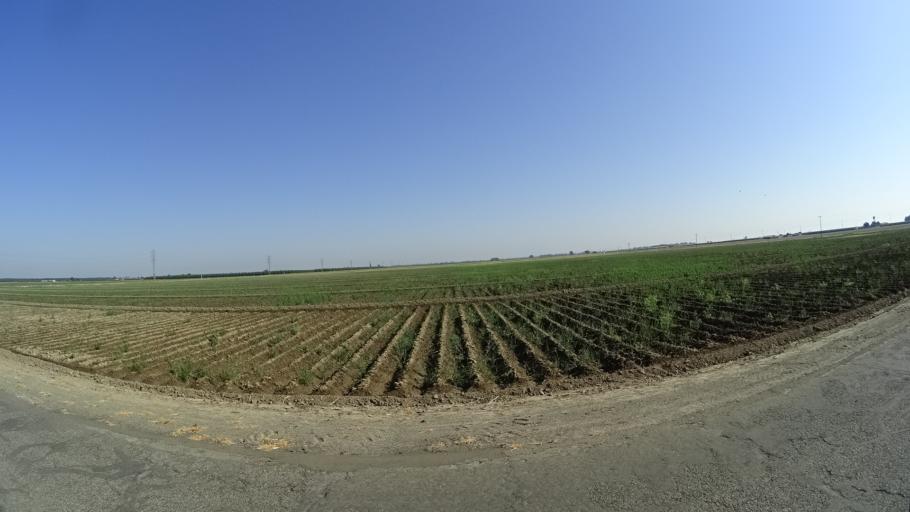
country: US
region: California
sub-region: Kings County
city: Lucerne
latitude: 36.3865
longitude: -119.5897
